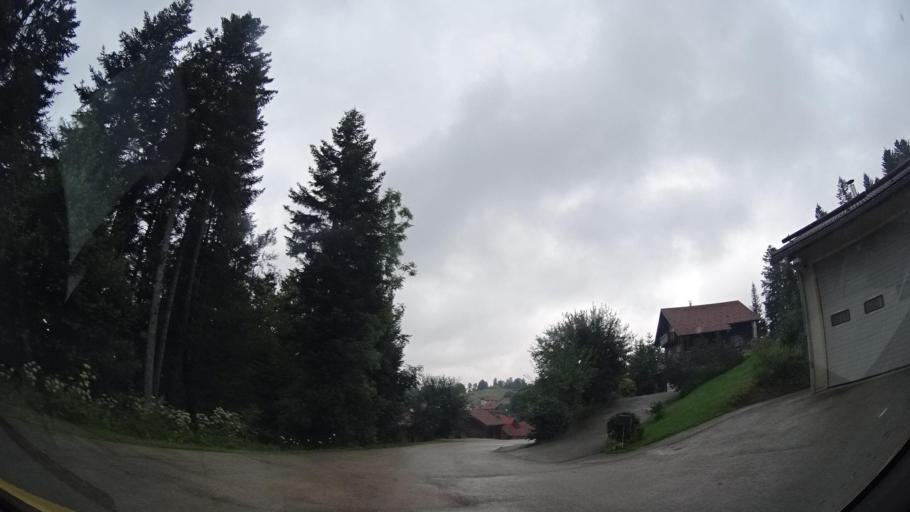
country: FR
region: Franche-Comte
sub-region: Departement du Doubs
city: Les Fourgs
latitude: 46.8242
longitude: 6.3393
